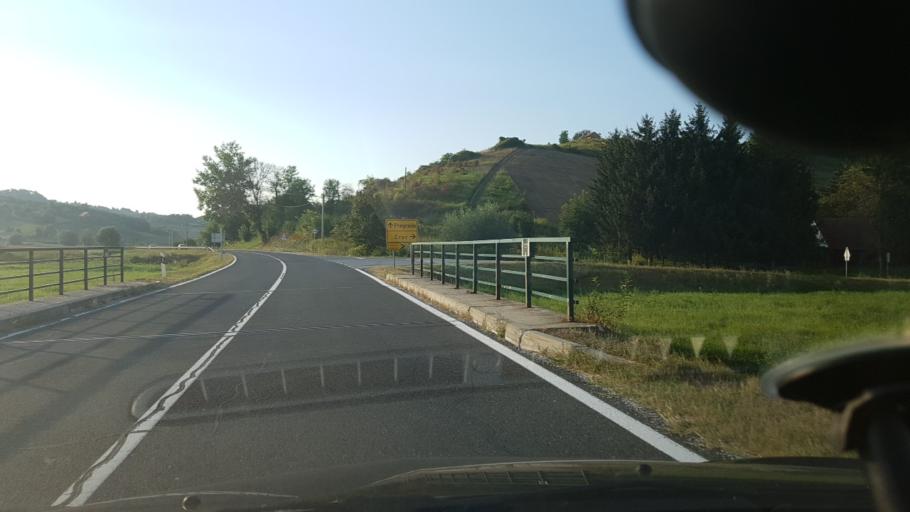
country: HR
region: Krapinsko-Zagorska
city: Pregrada
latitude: 46.1127
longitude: 15.8117
